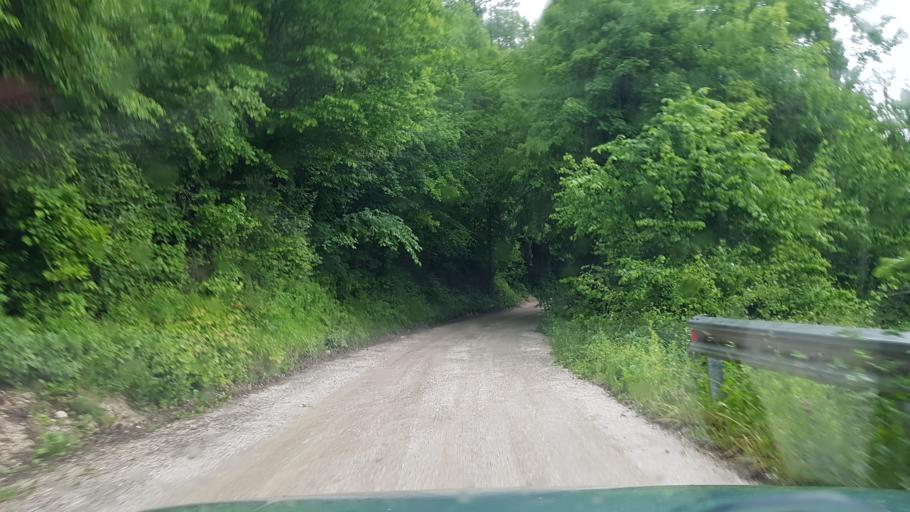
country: SI
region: Bled
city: Zasip
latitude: 46.3892
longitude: 14.1240
